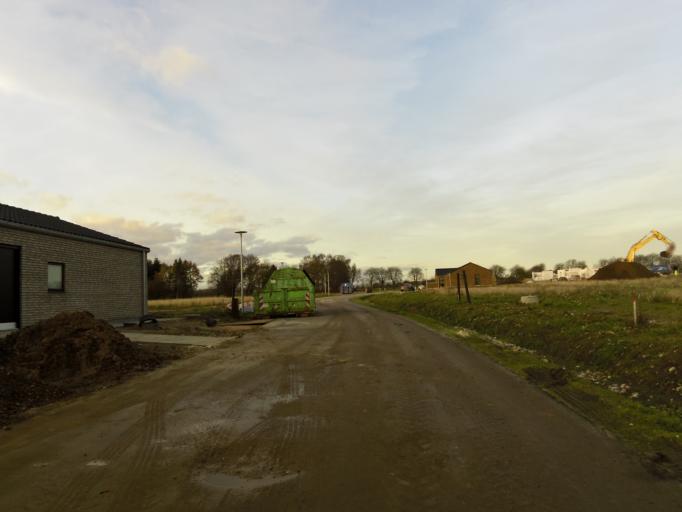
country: DK
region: South Denmark
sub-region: Vejen Kommune
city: Vejen
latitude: 55.4572
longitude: 9.1050
